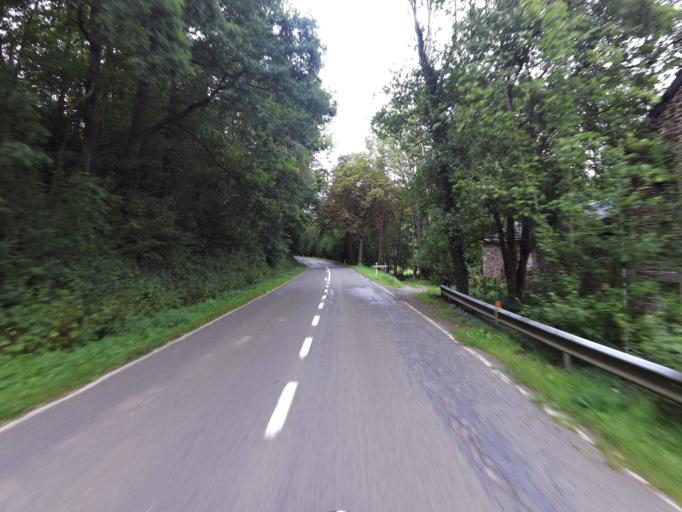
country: BE
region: Wallonia
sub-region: Province du Luxembourg
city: Erezee
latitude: 50.2914
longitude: 5.5476
